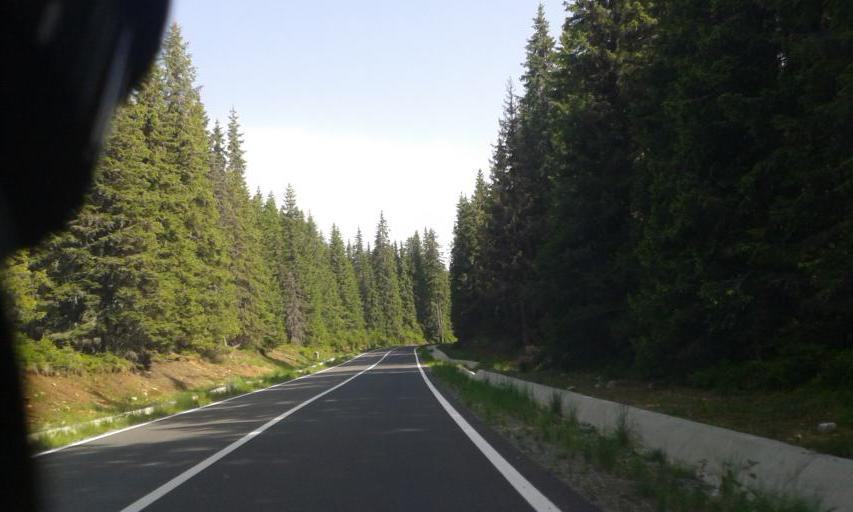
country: RO
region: Hunedoara
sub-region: Oras Petrila
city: Petrila
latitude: 45.4877
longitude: 23.6387
